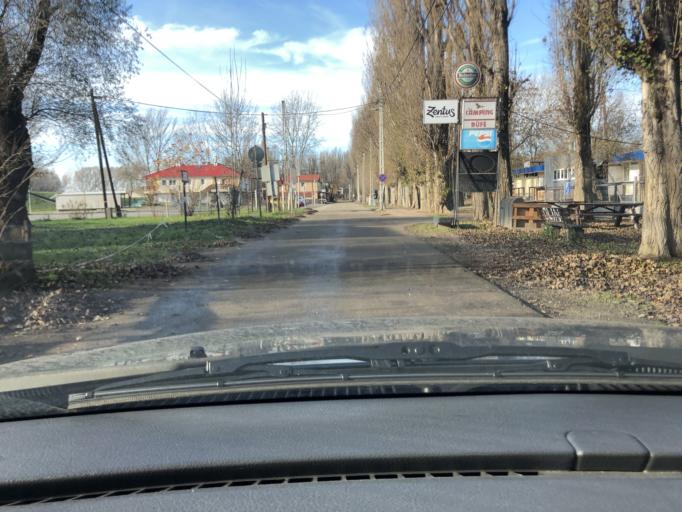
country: HU
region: Csongrad
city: Csongrad
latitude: 46.7148
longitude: 20.1856
